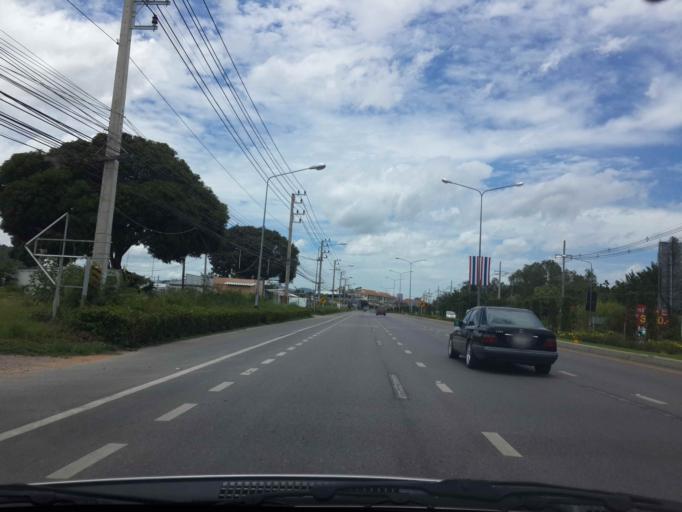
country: TH
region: Prachuap Khiri Khan
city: Hua Hin
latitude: 12.6322
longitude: 99.9495
